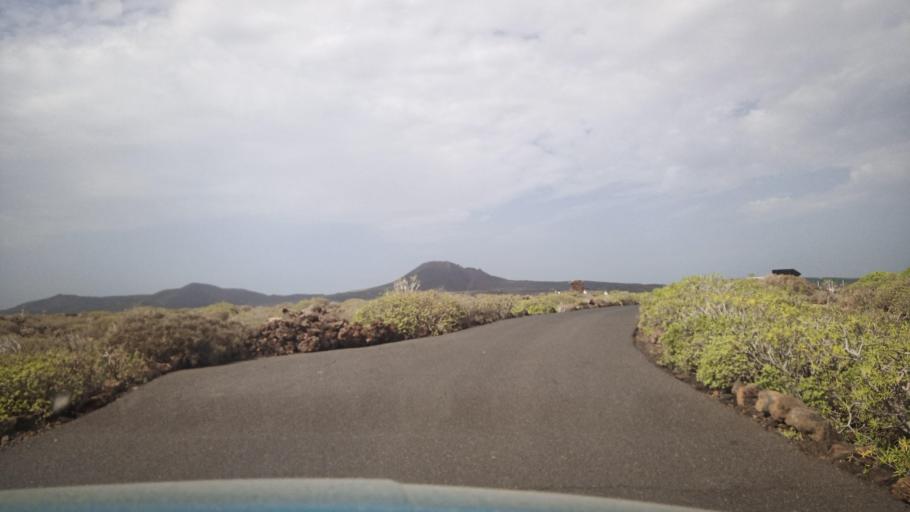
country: ES
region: Canary Islands
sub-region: Provincia de Las Palmas
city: Haria
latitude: 29.1600
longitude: -13.4383
